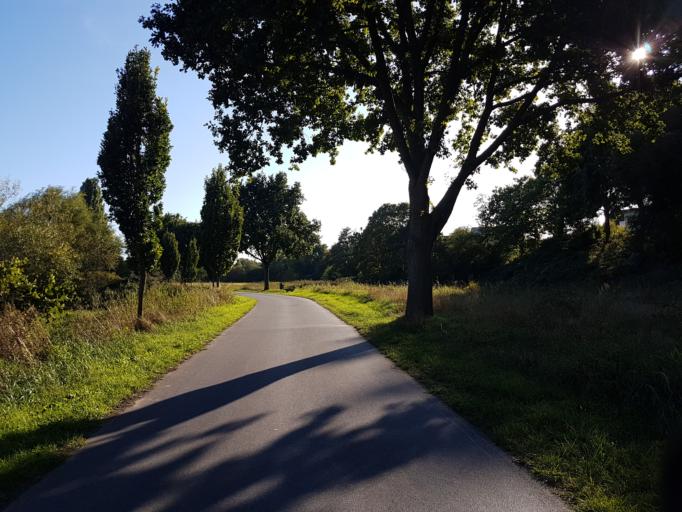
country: DE
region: North Rhine-Westphalia
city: Bad Oeynhausen
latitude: 52.2234
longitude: 8.8280
